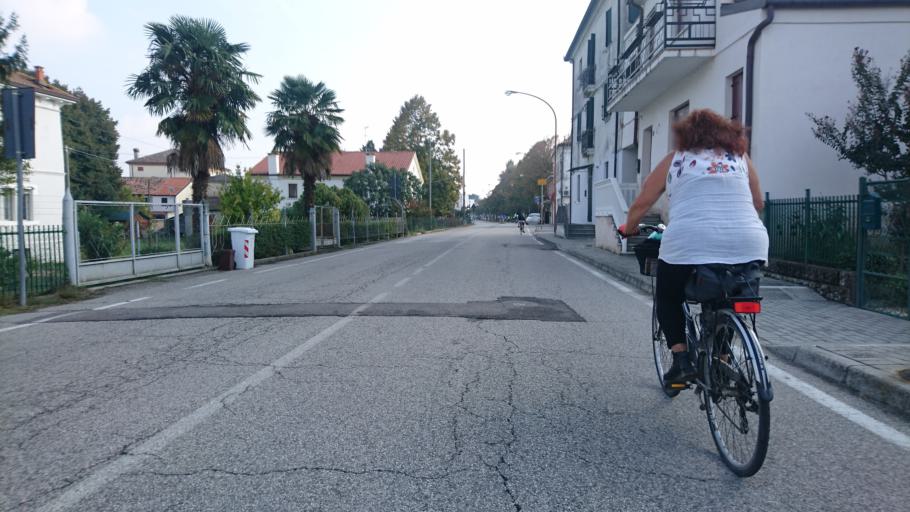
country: IT
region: Veneto
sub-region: Provincia di Rovigo
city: Polesella
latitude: 44.9651
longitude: 11.7498
